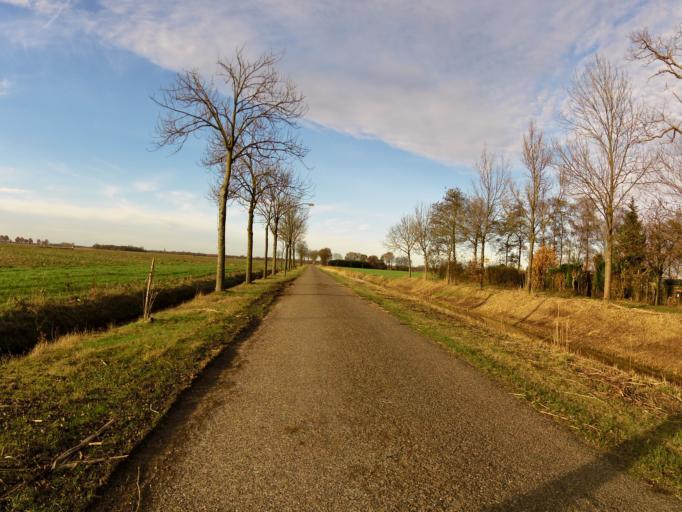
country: NL
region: North Brabant
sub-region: Gemeente Vught
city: Vught
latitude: 51.6679
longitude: 5.2735
